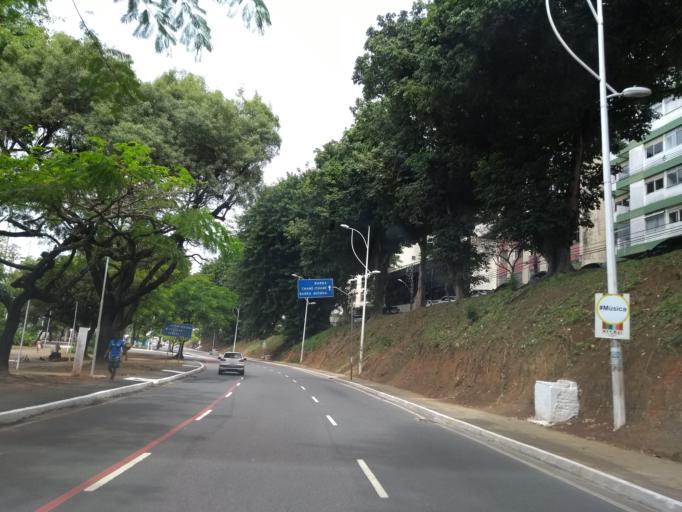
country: BR
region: Bahia
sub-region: Salvador
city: Salvador
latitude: -13.0009
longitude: -38.5203
